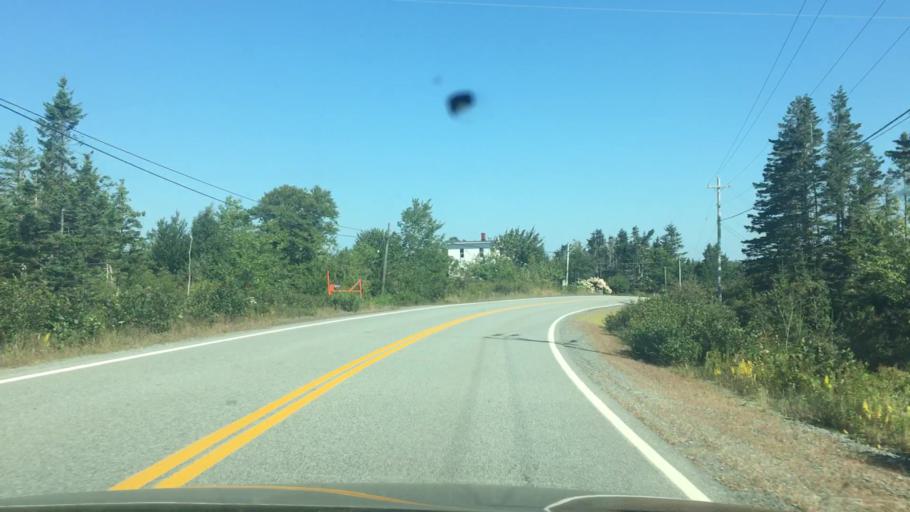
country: CA
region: Nova Scotia
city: Cole Harbour
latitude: 44.7980
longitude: -62.7163
